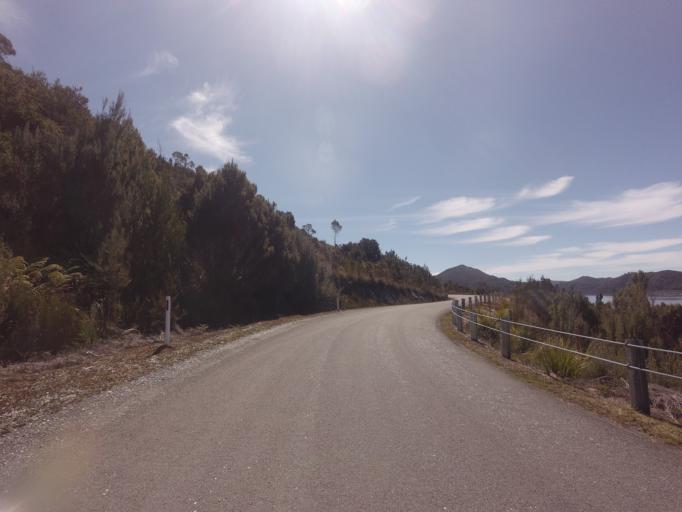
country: AU
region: Tasmania
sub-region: West Coast
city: Queenstown
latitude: -42.7379
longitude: 145.9815
